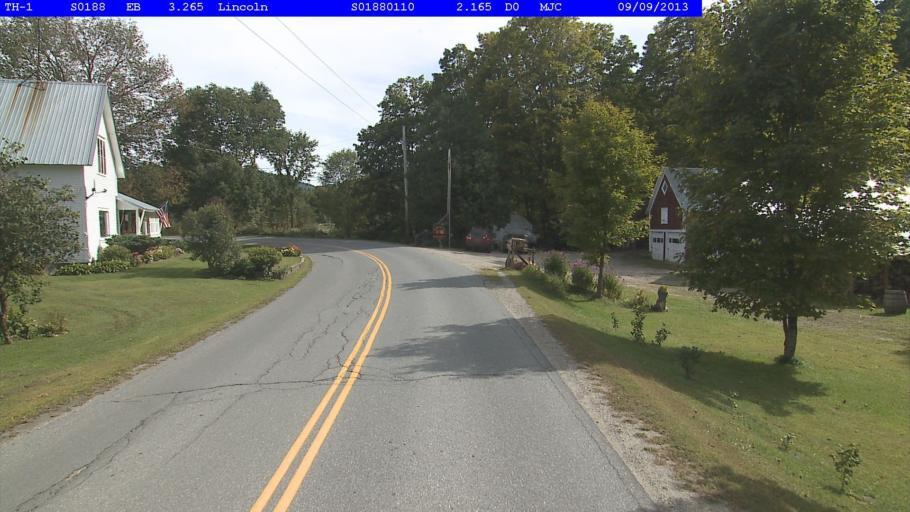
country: US
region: Vermont
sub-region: Addison County
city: Bristol
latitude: 44.1062
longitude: -72.9989
